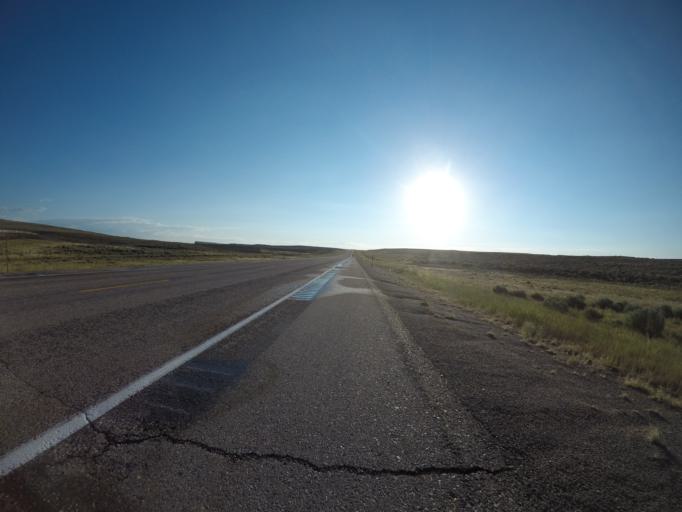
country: US
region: Wyoming
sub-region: Lincoln County
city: Kemmerer
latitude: 41.8723
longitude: -110.4515
